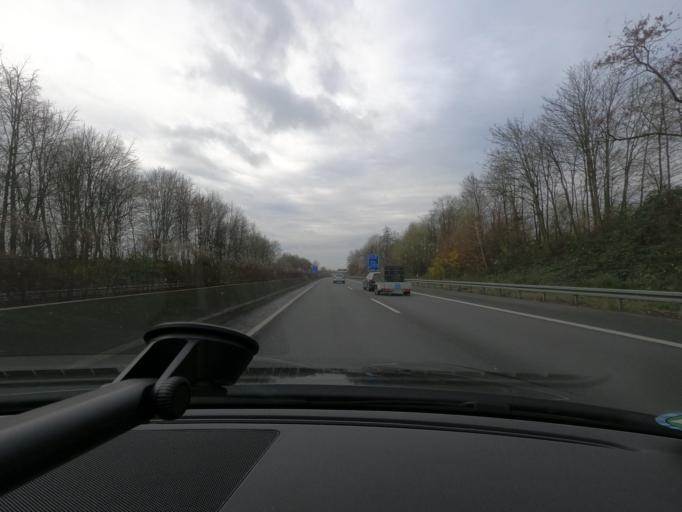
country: DE
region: North Rhine-Westphalia
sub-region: Regierungsbezirk Dusseldorf
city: Muelheim (Ruhr)
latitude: 51.3657
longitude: 6.8824
